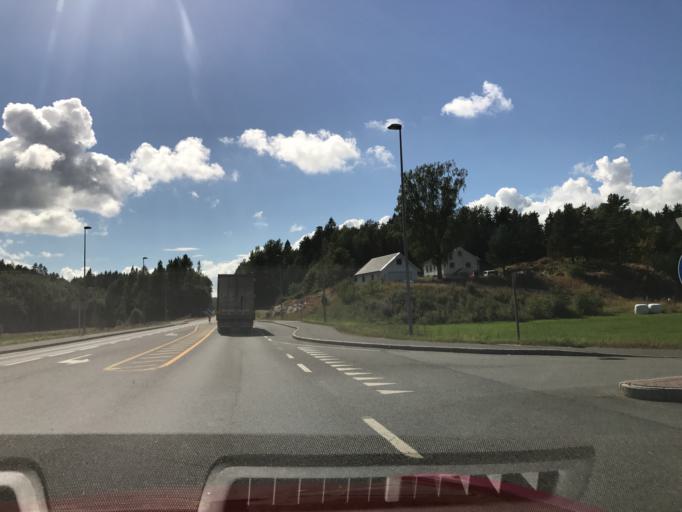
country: NO
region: Telemark
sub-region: Bamble
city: Herre
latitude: 58.9715
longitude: 9.5724
